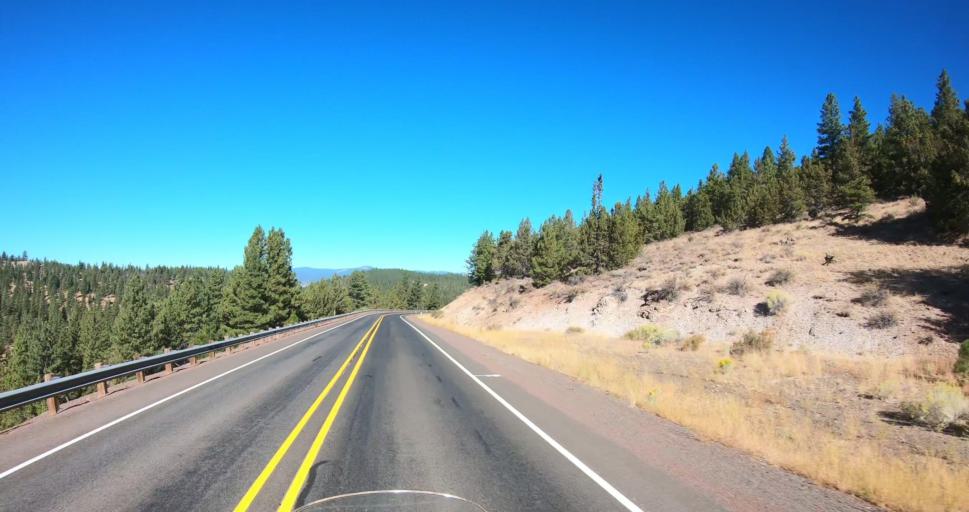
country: US
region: Oregon
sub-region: Lake County
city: Lakeview
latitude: 42.2415
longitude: -120.3086
